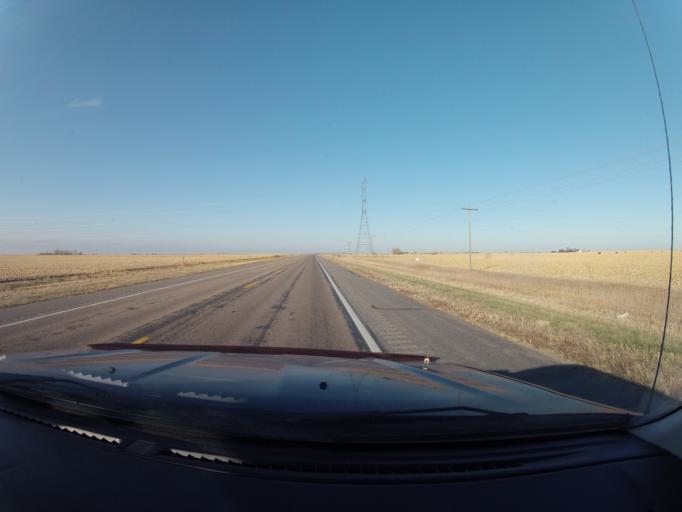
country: US
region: Nebraska
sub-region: Kearney County
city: Minden
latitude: 40.5444
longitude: -98.9518
